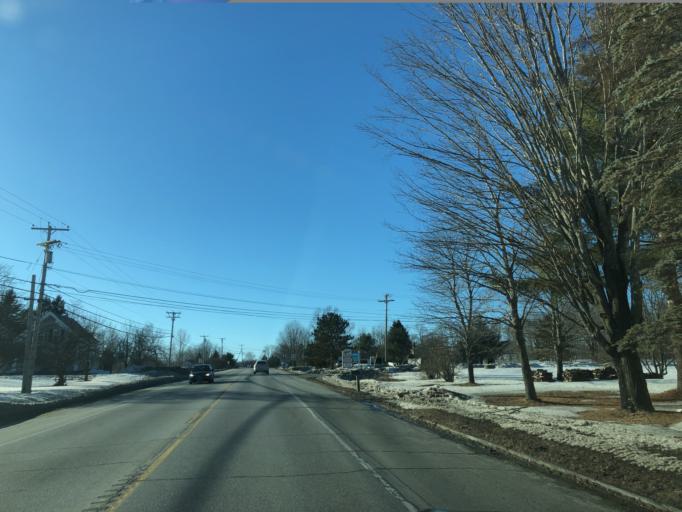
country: US
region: Maine
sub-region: Penobscot County
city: Charleston
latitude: 44.9879
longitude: -69.0115
